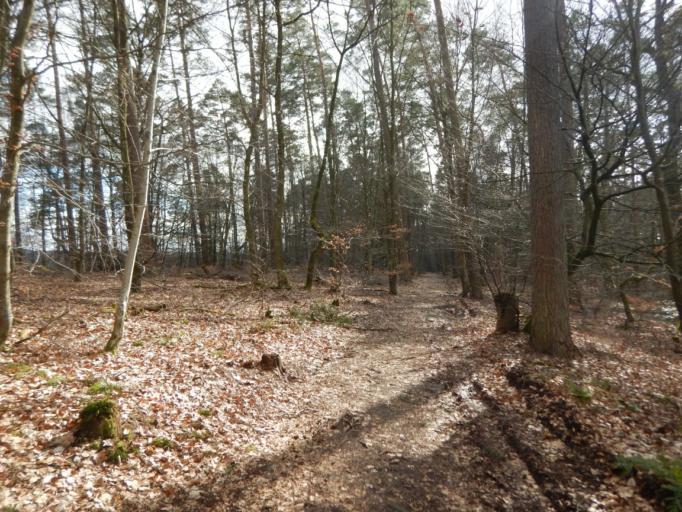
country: LU
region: Grevenmacher
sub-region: Canton d'Echternach
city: Beaufort
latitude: 49.8273
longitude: 6.3216
